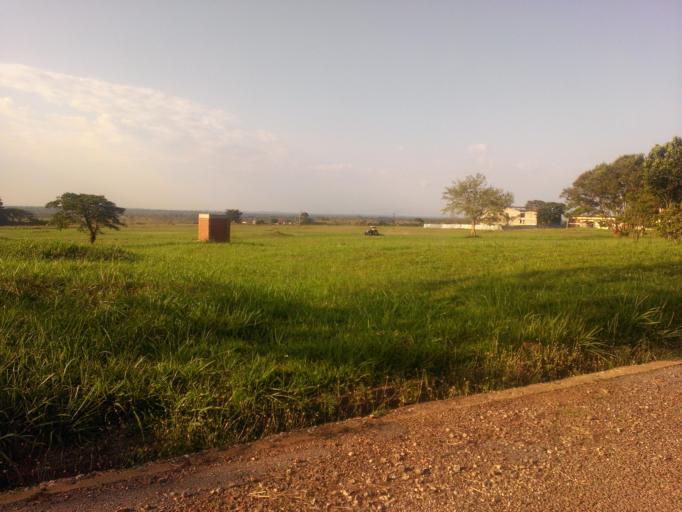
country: UG
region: Eastern Region
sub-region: Busia District
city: Busia
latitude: 0.5452
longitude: 34.0189
